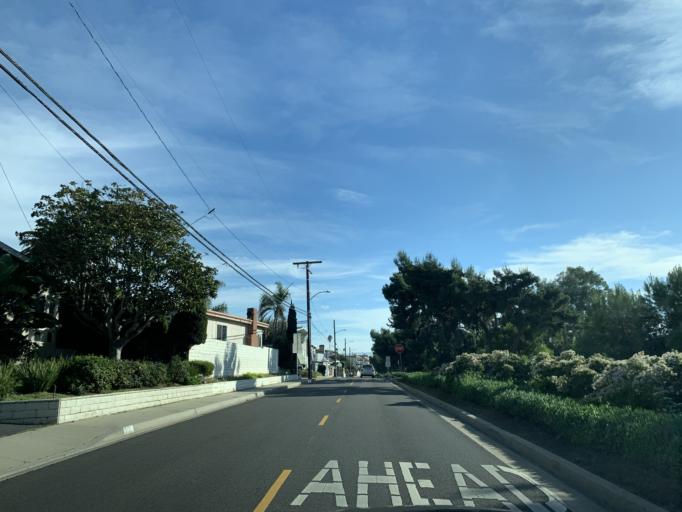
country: US
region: California
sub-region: Los Angeles County
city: Hermosa Beach
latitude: 33.8703
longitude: -118.3972
